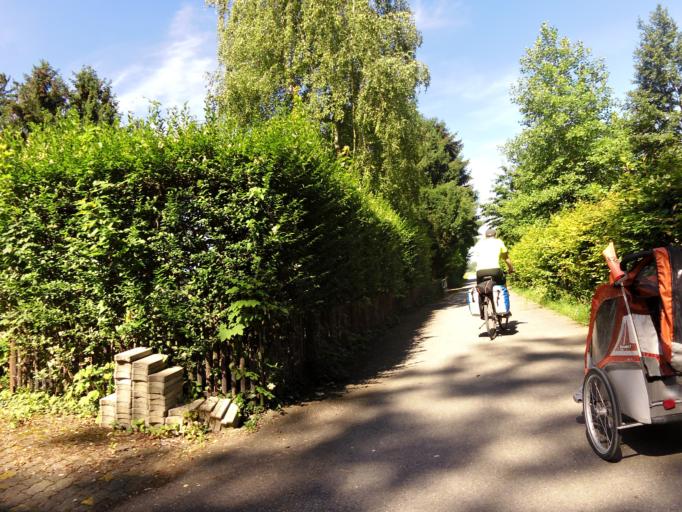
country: CH
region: Thurgau
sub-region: Kreuzlingen District
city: Gottlieben
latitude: 47.6618
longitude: 9.1346
